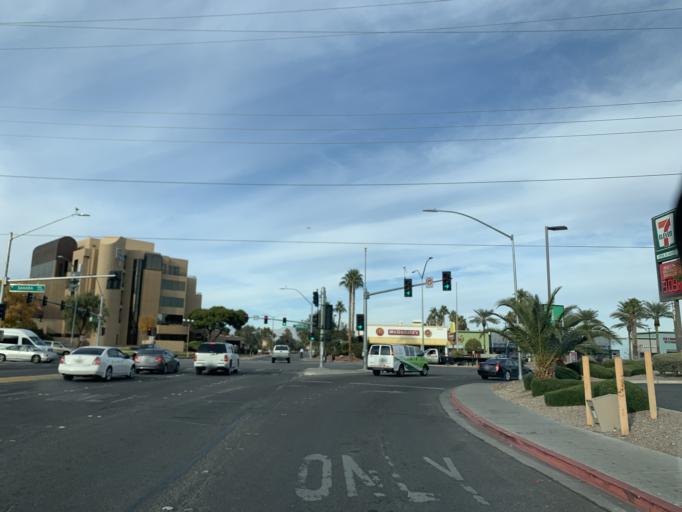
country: US
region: Nevada
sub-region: Clark County
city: Las Vegas
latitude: 36.1438
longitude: -115.1774
